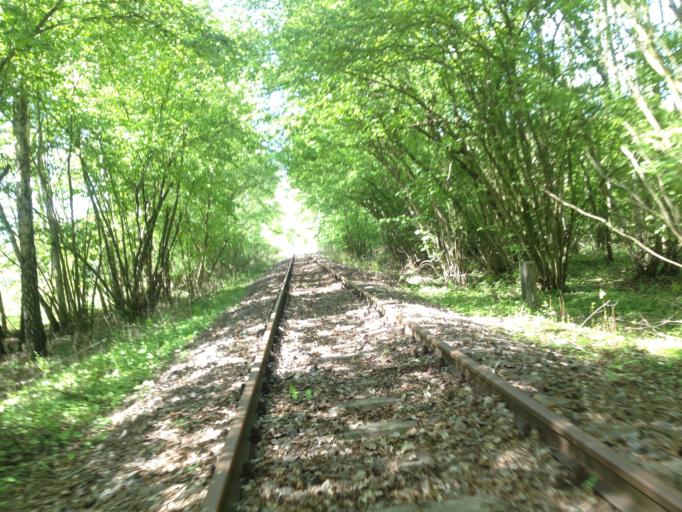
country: DE
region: Brandenburg
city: Templin
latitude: 53.1279
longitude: 13.4427
